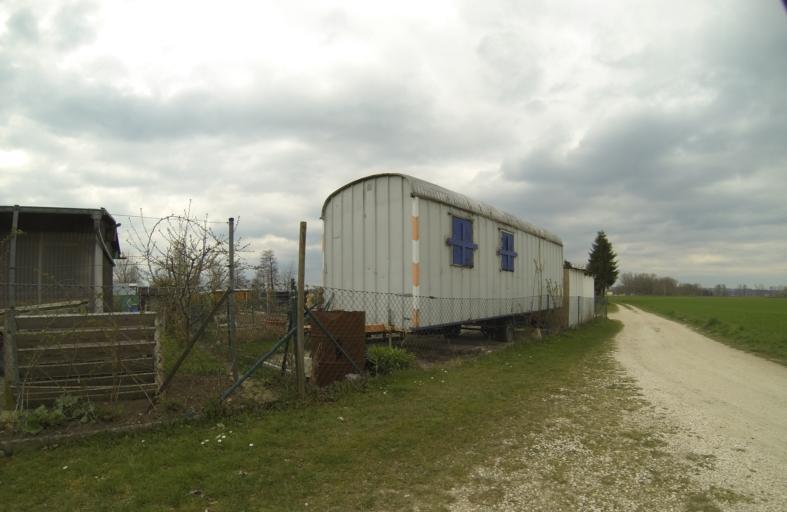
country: DE
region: Baden-Wuerttemberg
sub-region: Tuebingen Region
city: Erbach
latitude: 48.3066
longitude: 9.9007
